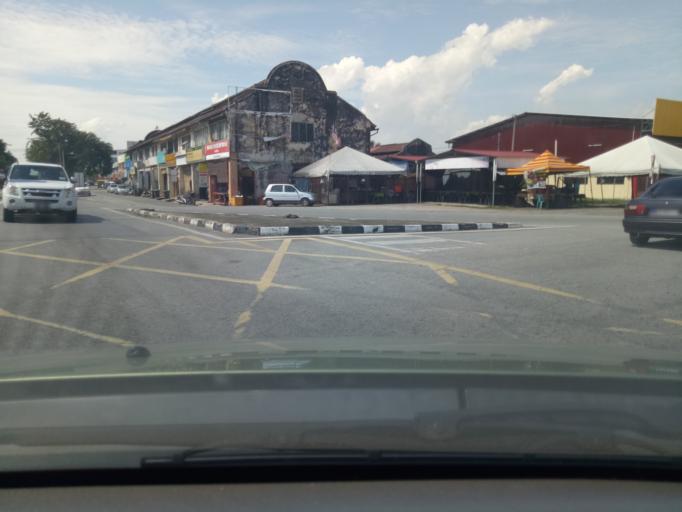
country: MY
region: Kedah
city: Alor Setar
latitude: 5.9733
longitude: 100.4003
